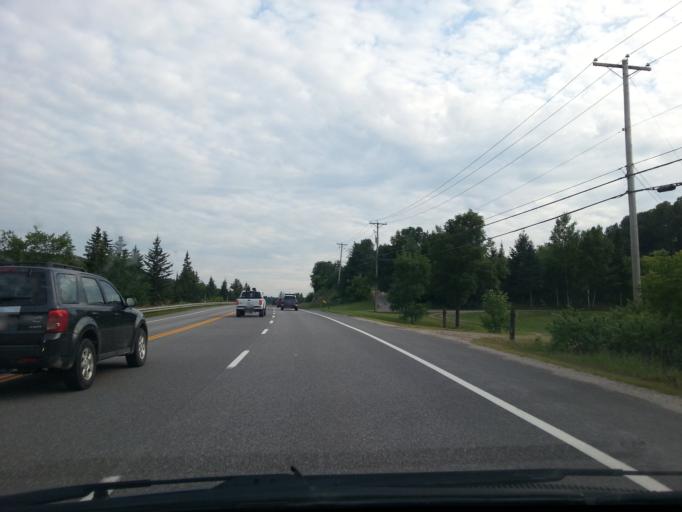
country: CA
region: Quebec
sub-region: Outaouais
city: Wakefield
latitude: 45.7268
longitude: -75.9103
